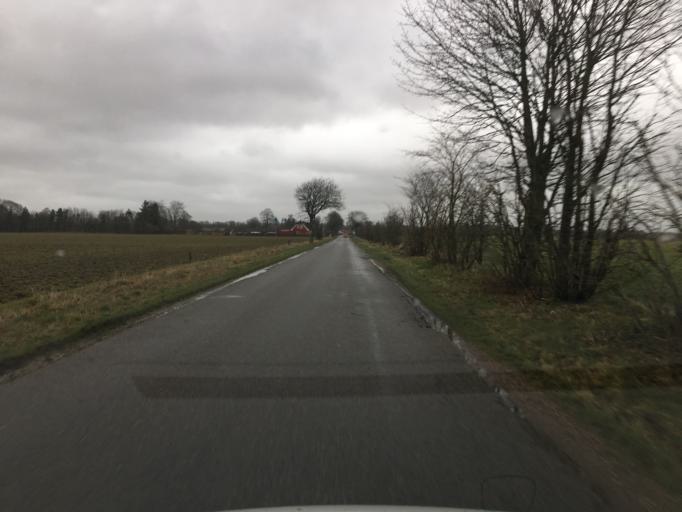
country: DK
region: South Denmark
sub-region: Aabenraa Kommune
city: Tinglev
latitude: 54.9036
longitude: 9.2613
